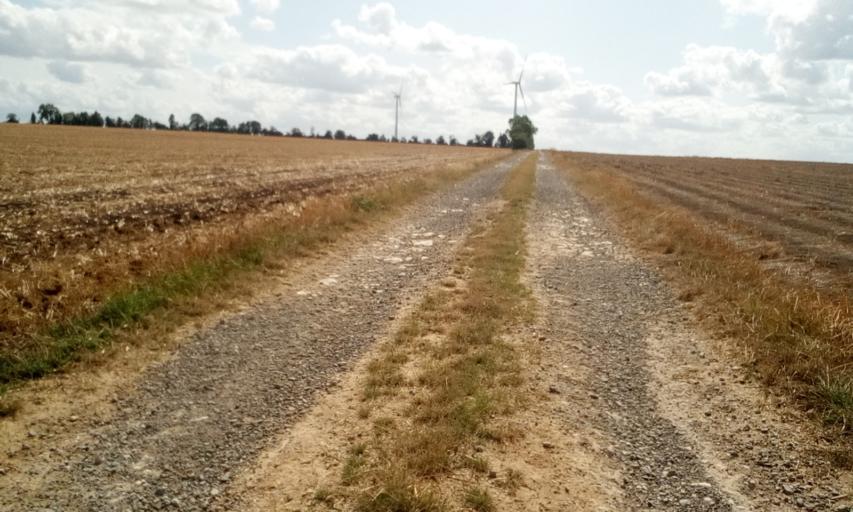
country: FR
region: Lower Normandy
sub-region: Departement du Calvados
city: Bellengreville
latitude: 49.1026
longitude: -0.2207
